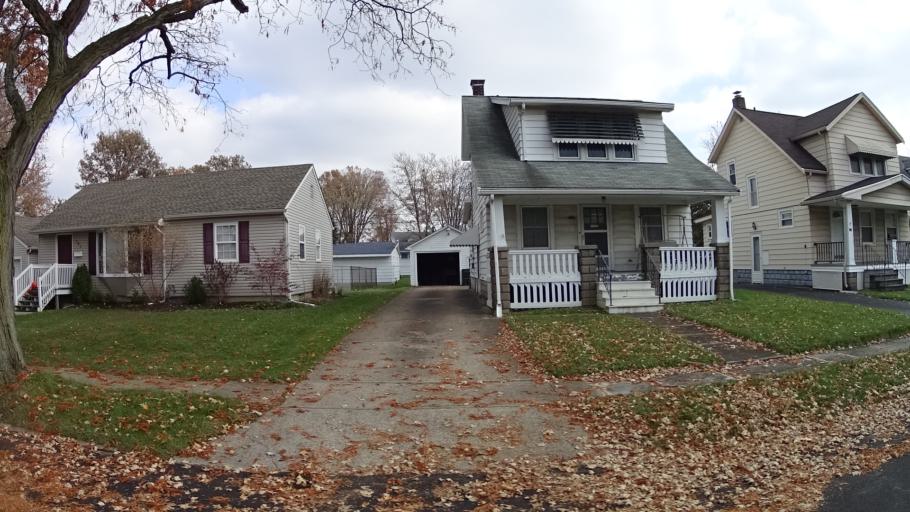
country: US
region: Ohio
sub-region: Lorain County
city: Elyria
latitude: 41.3775
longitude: -82.0805
